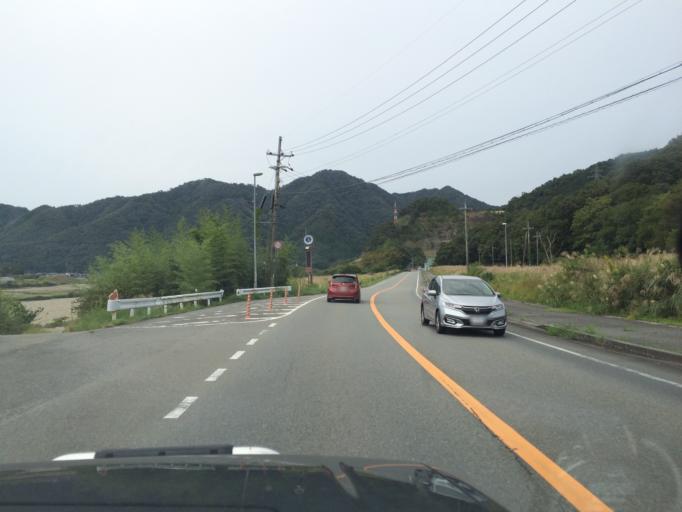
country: JP
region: Hyogo
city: Toyooka
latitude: 35.4007
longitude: 134.7852
